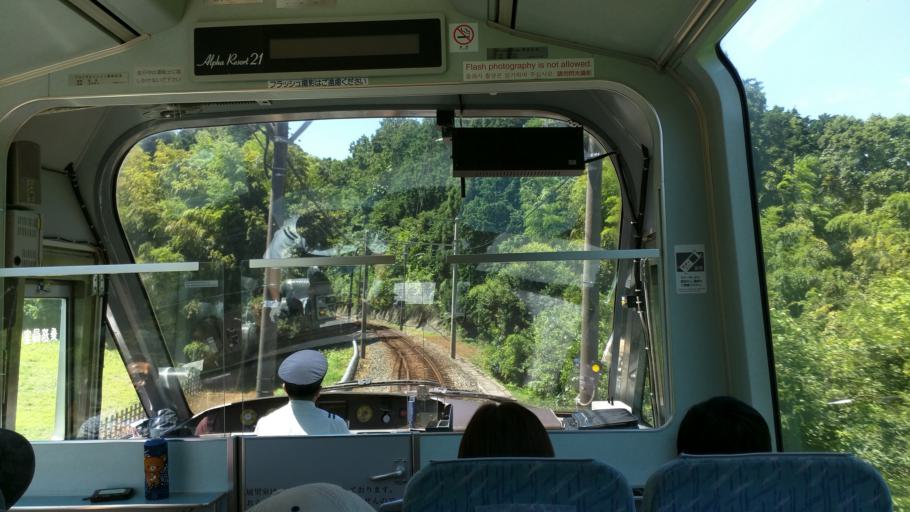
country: JP
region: Shizuoka
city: Ito
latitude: 34.9213
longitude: 139.1335
